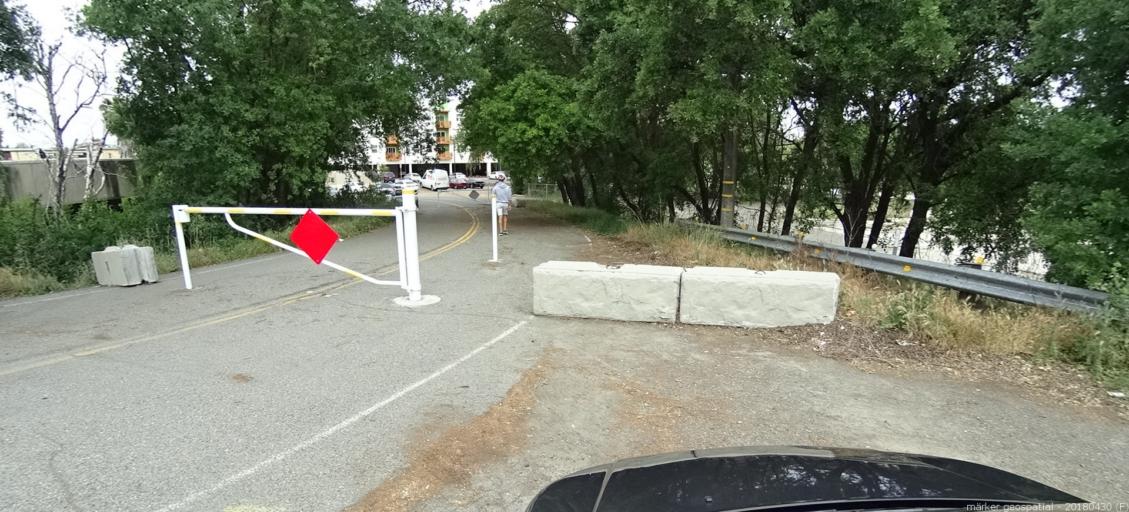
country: US
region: California
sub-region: Yolo County
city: West Sacramento
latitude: 38.5809
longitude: -121.5158
